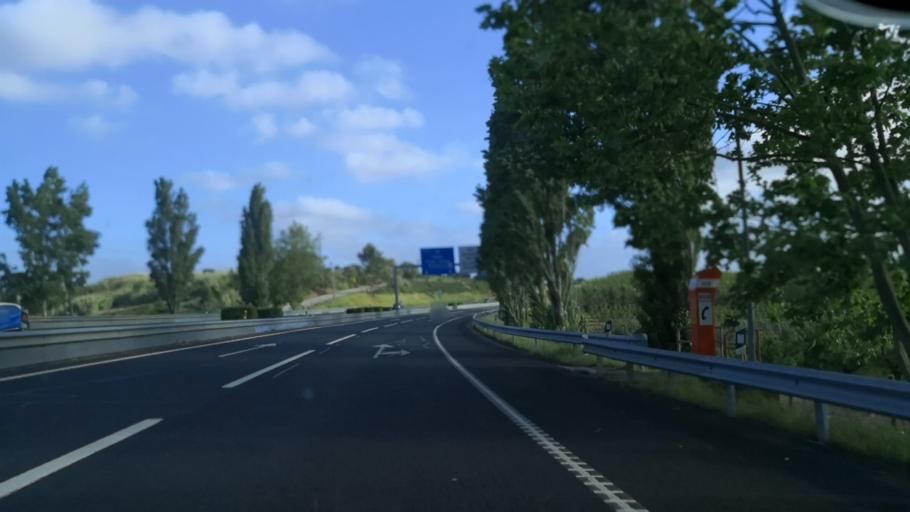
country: PT
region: Leiria
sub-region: Bombarral
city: Bombarral
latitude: 39.2935
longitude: -9.1578
